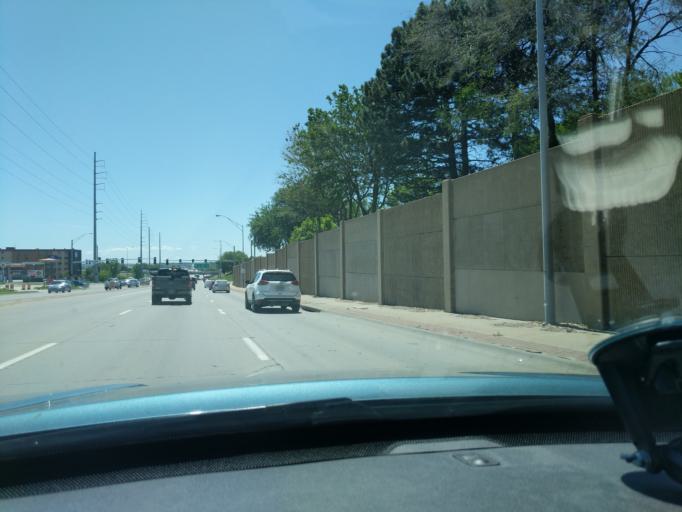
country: US
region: Nebraska
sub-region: Douglas County
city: Ralston
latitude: 41.2284
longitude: -96.0240
